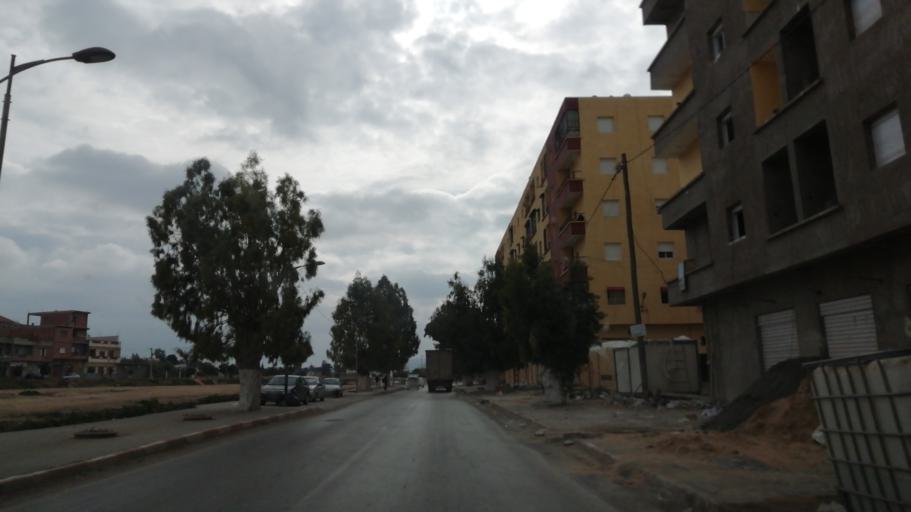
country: DZ
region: Oran
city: Sidi ech Chahmi
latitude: 35.5569
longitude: -0.4480
